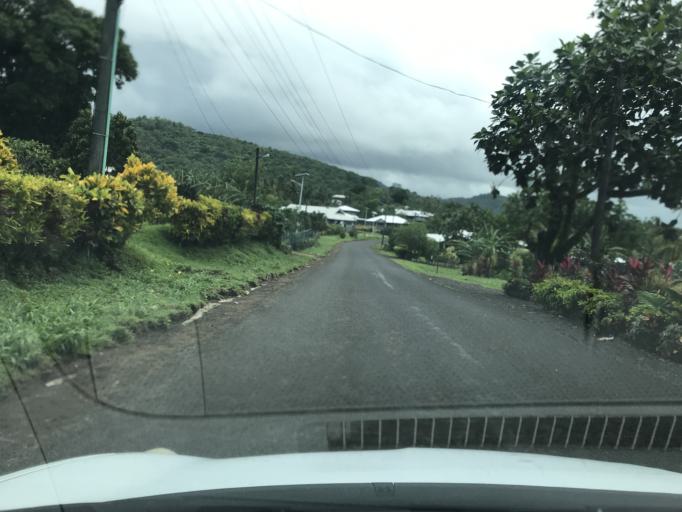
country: WS
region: Atua
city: Lufilufi
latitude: -13.8760
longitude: -171.6025
